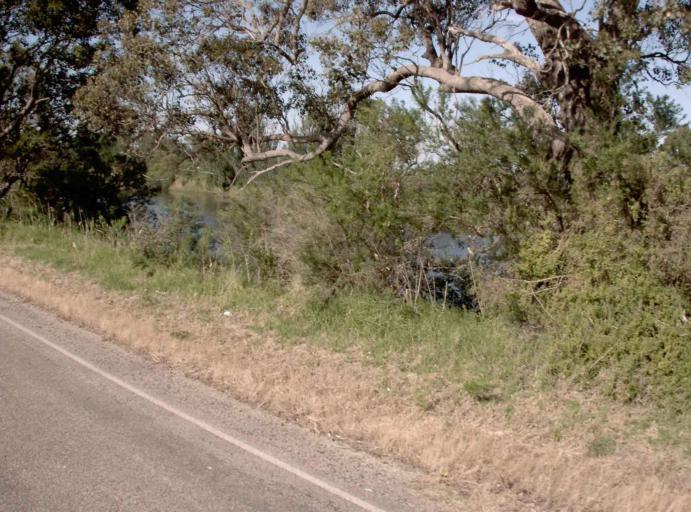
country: AU
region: Victoria
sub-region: East Gippsland
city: Lakes Entrance
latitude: -37.8359
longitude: 147.8616
